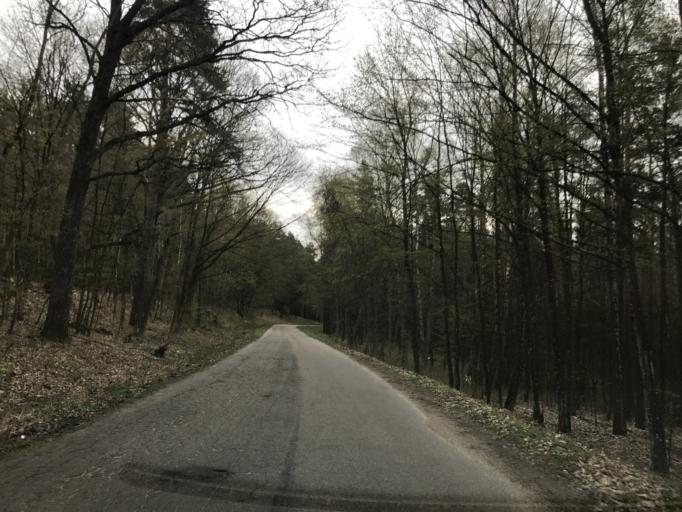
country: PL
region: Warmian-Masurian Voivodeship
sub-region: Powiat ostrodzki
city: Gierzwald
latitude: 53.6329
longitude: 20.1272
